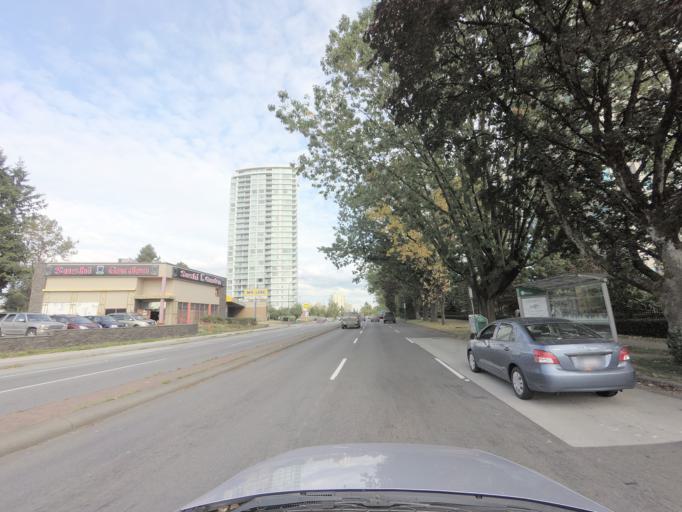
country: CA
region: British Columbia
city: Burnaby
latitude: 49.2186
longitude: -122.9664
